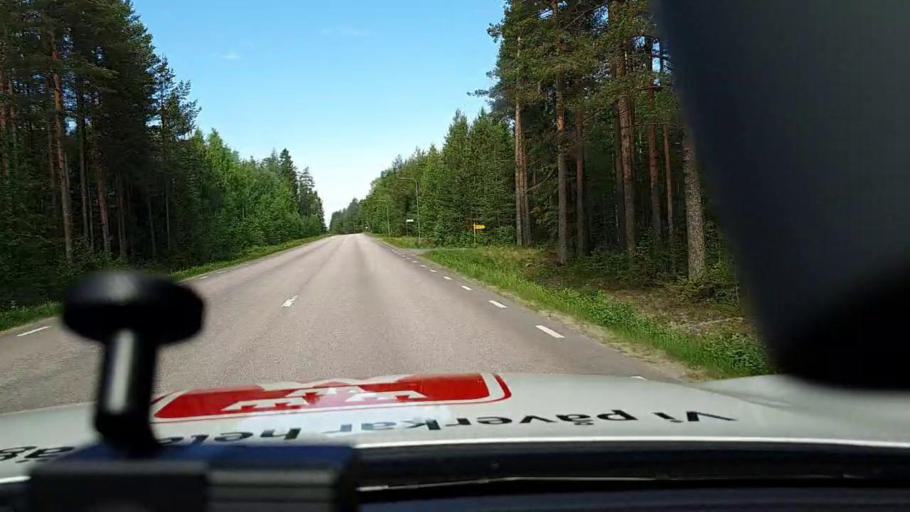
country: SE
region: Norrbotten
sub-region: Lulea Kommun
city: Sodra Sunderbyn
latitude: 65.6461
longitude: 21.8831
